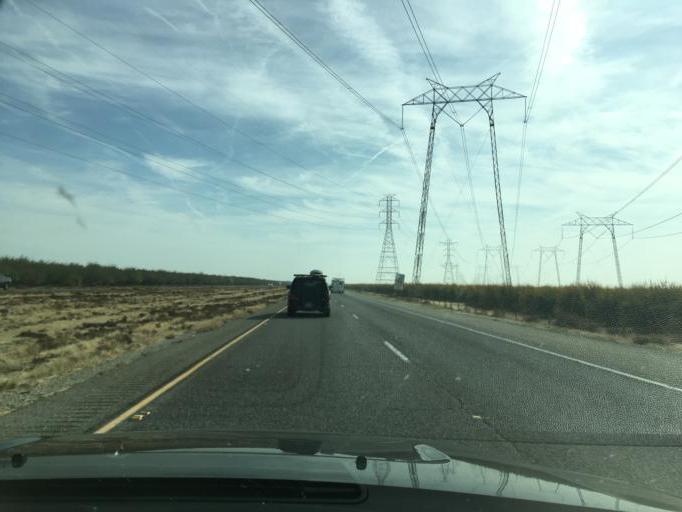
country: US
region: California
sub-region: Kern County
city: Buttonwillow
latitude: 35.4933
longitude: -119.5273
